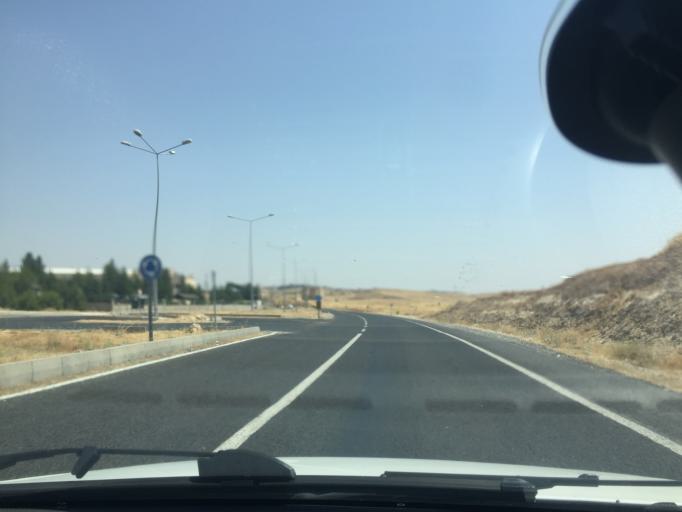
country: TR
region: Mardin
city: Acirli
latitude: 37.4391
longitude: 41.2957
